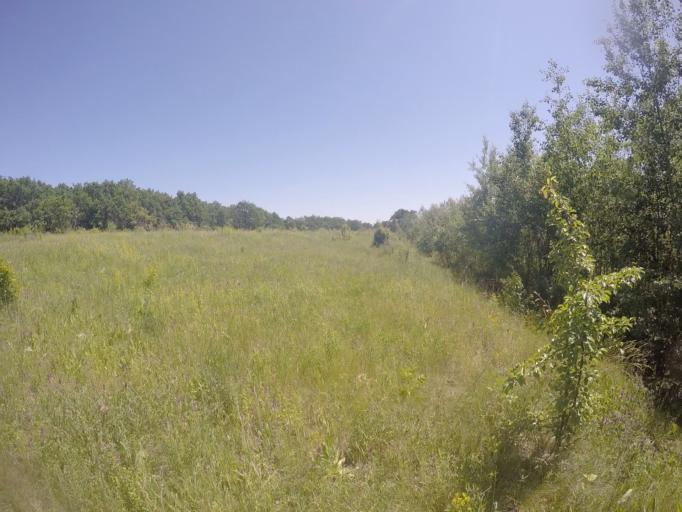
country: RU
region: Saratov
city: Krasnyy Oktyabr'
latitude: 51.3102
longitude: 45.5498
